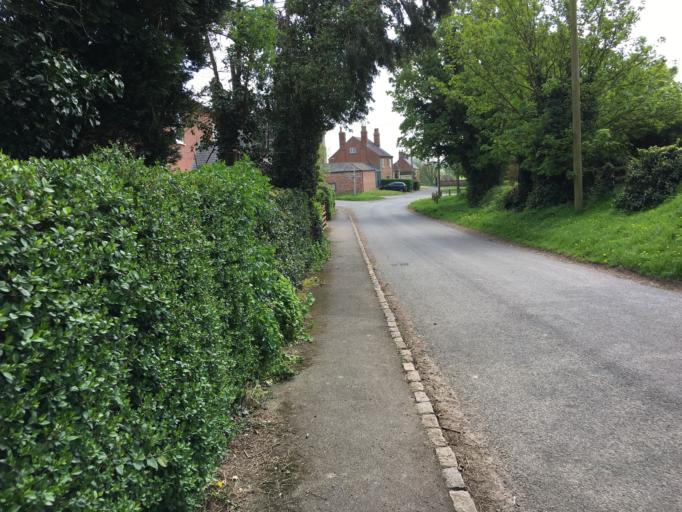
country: GB
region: England
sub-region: Leicestershire
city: Houghton on the Hill
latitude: 52.5986
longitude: -0.9855
